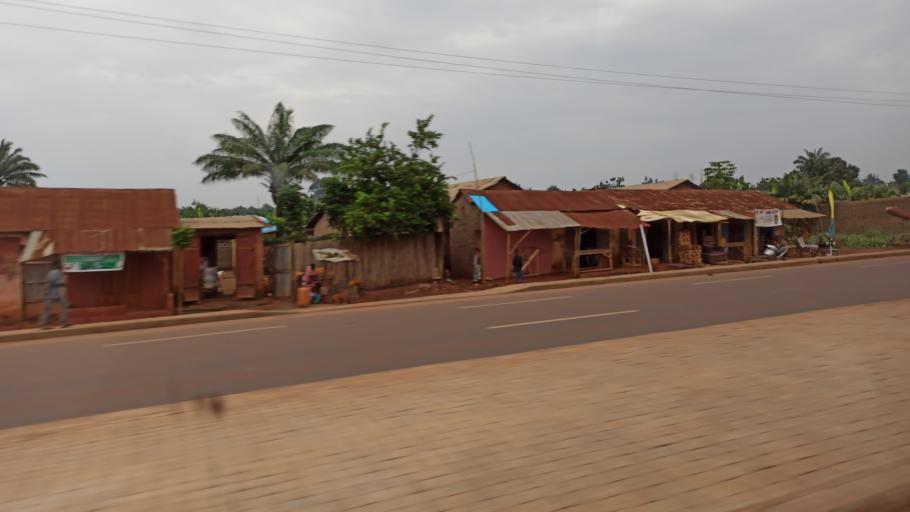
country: BJ
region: Queme
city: Porto-Novo
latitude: 6.5337
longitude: 2.5980
